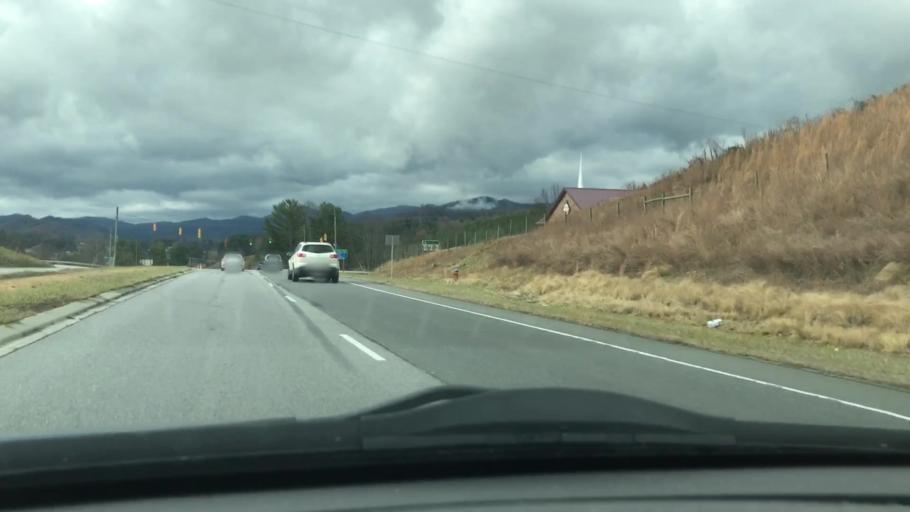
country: US
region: North Carolina
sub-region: Yancey County
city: Burnsville
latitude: 35.9126
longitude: -82.3326
